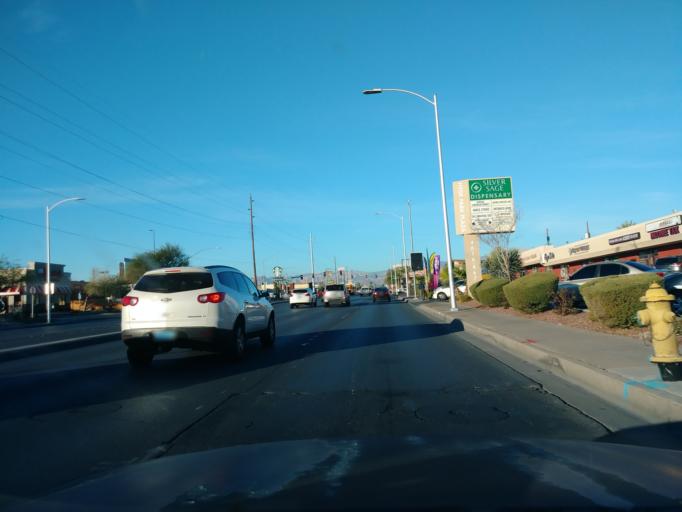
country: US
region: Nevada
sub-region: Clark County
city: Spring Valley
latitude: 36.1592
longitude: -115.2038
